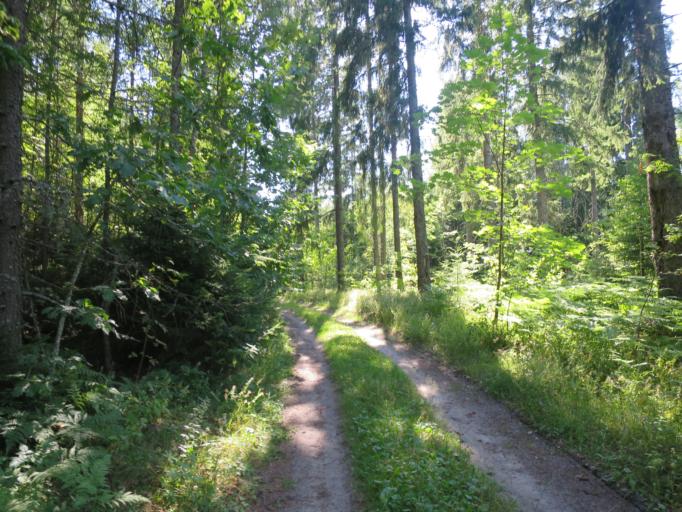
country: LV
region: Sigulda
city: Sigulda
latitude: 57.1067
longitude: 24.8121
